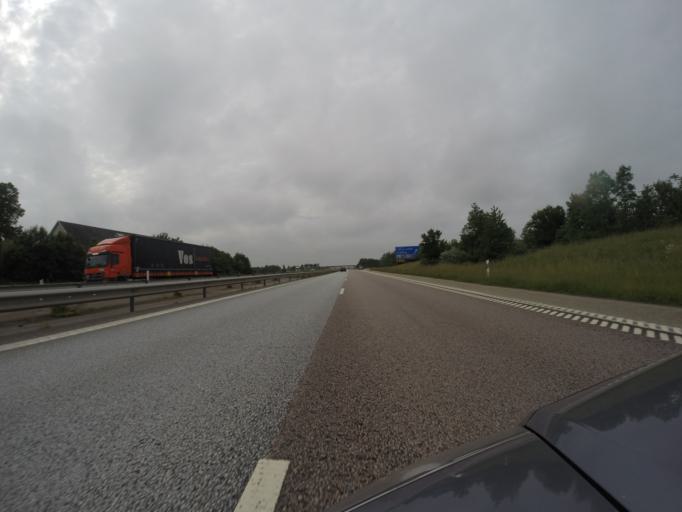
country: SE
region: Skane
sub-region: Lomma Kommun
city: Lomma
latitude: 55.6909
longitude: 13.0975
